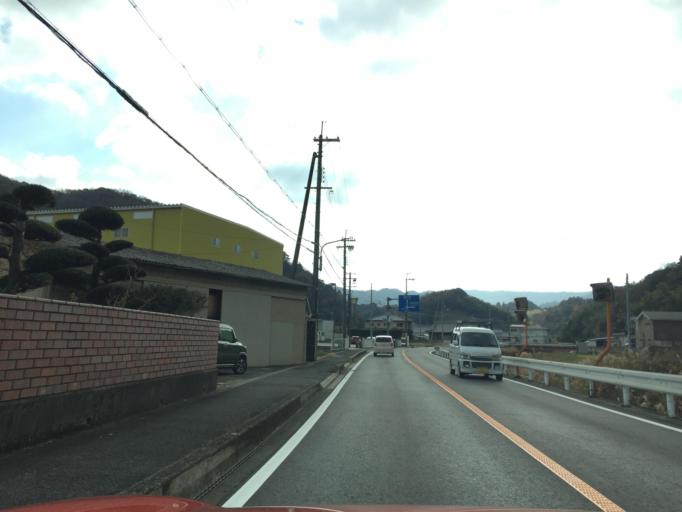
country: JP
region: Wakayama
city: Kainan
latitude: 34.1705
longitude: 135.2507
